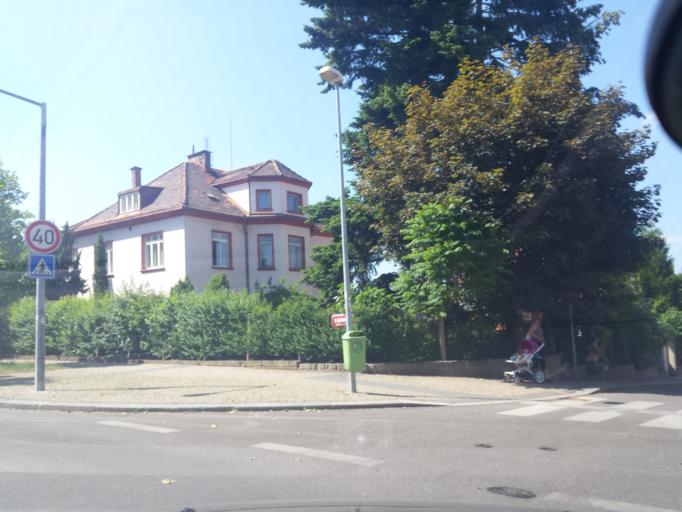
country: CZ
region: Praha
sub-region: Praha 1
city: Mala Strana
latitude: 50.0942
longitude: 14.3838
